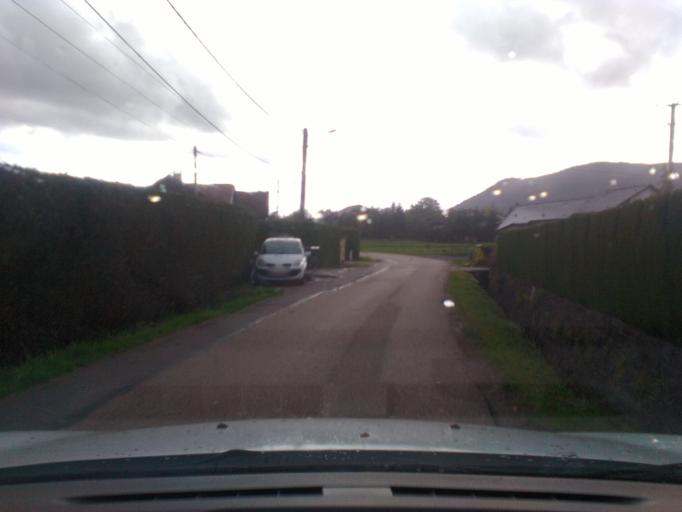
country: FR
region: Lorraine
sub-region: Departement des Vosges
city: Saint-Die-des-Vosges
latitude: 48.3109
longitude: 6.9331
